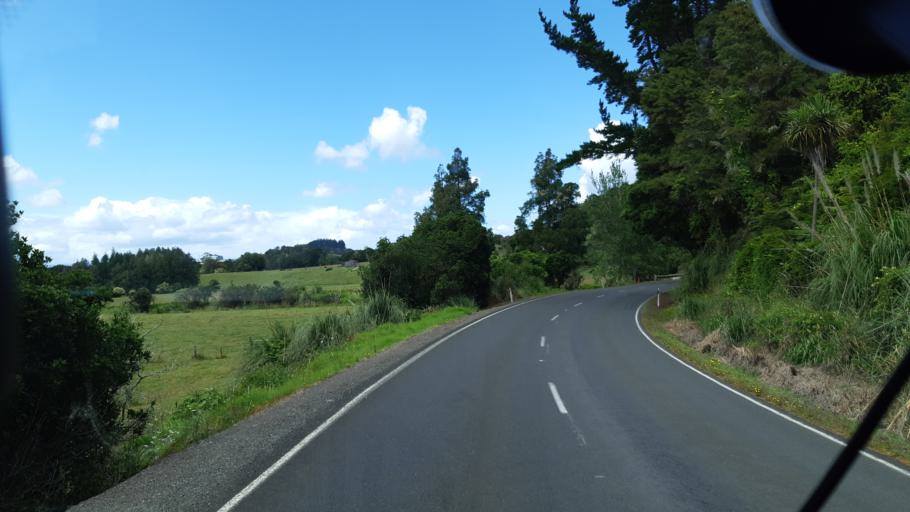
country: NZ
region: Northland
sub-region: Far North District
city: Taipa
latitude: -35.2604
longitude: 173.5276
